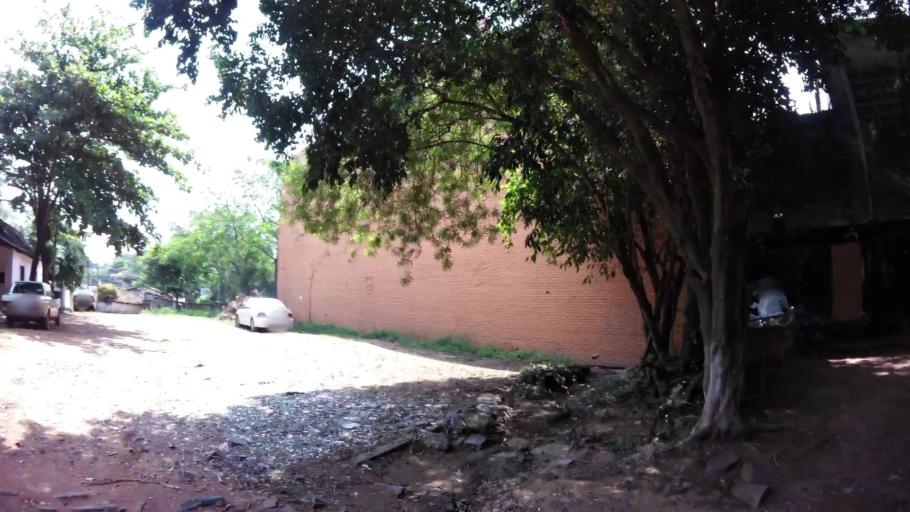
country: PY
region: Asuncion
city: Asuncion
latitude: -25.2827
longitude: -57.6086
